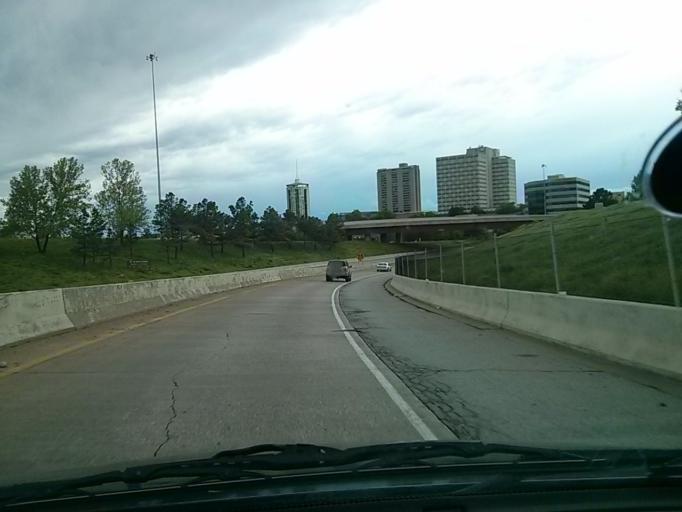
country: US
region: Oklahoma
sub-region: Tulsa County
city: Tulsa
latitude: 36.1430
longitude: -95.9810
